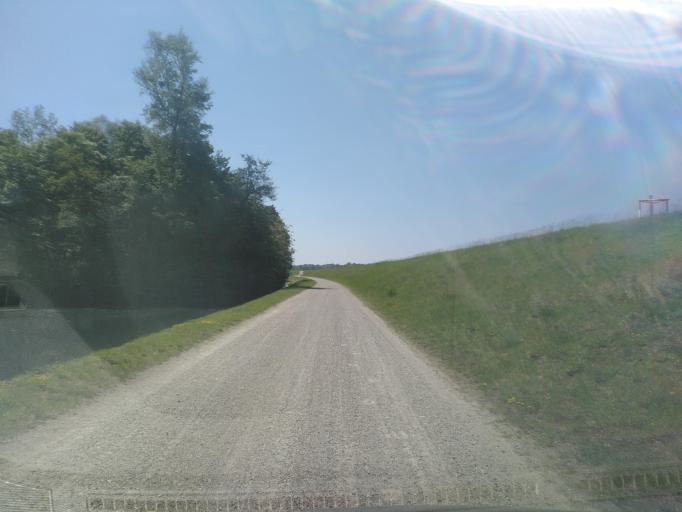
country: FR
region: Alsace
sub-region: Departement du Haut-Rhin
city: Kunheim
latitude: 48.0871
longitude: 7.5729
